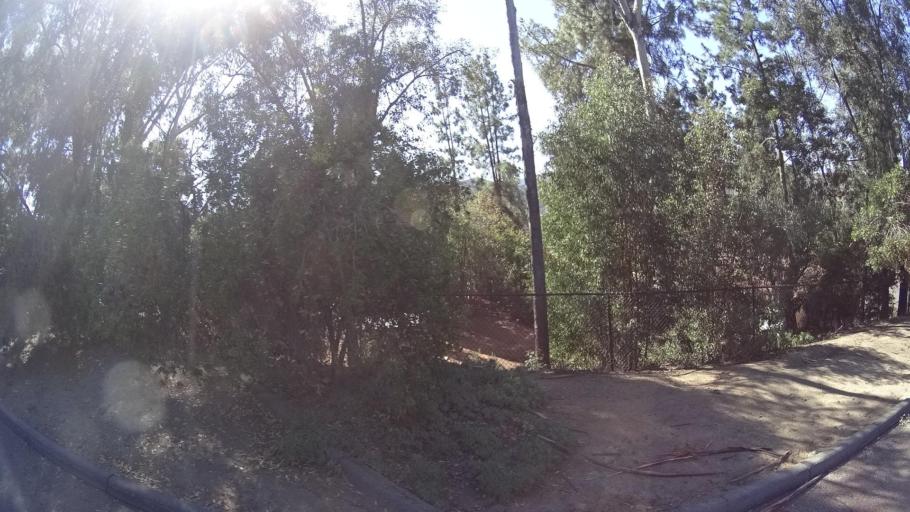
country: US
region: California
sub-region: San Diego County
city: Rancho San Diego
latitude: 32.7303
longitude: -116.9132
